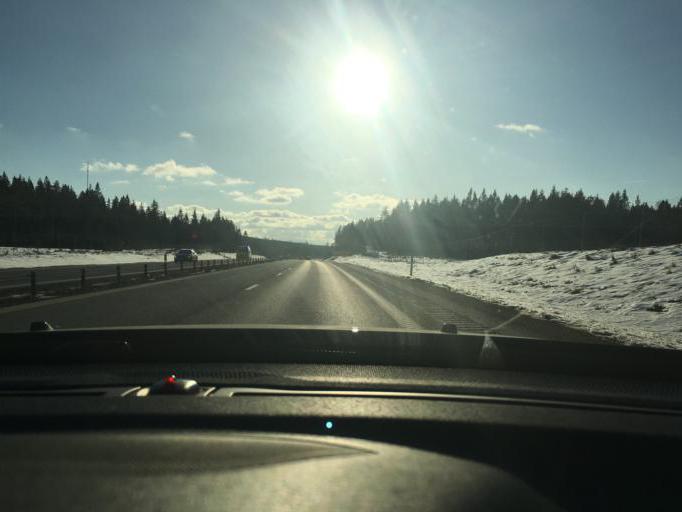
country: SE
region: Vaestra Goetaland
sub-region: Boras Kommun
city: Dalsjofors
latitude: 57.7499
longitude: 13.0725
